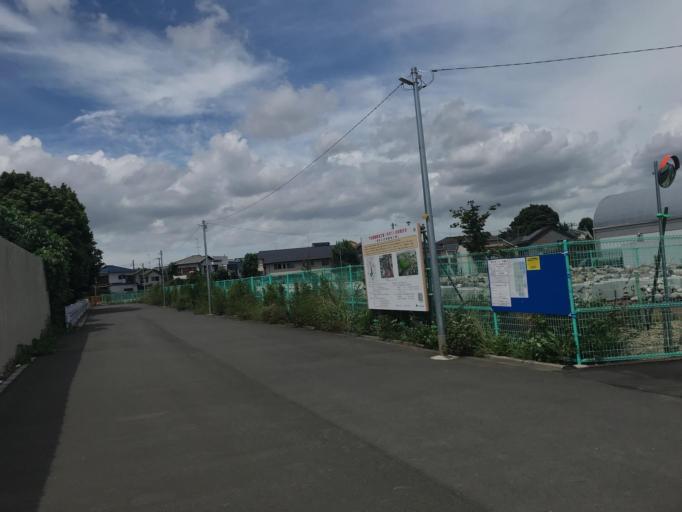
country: JP
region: Tokyo
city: Tanashicho
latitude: 35.7624
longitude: 139.5453
